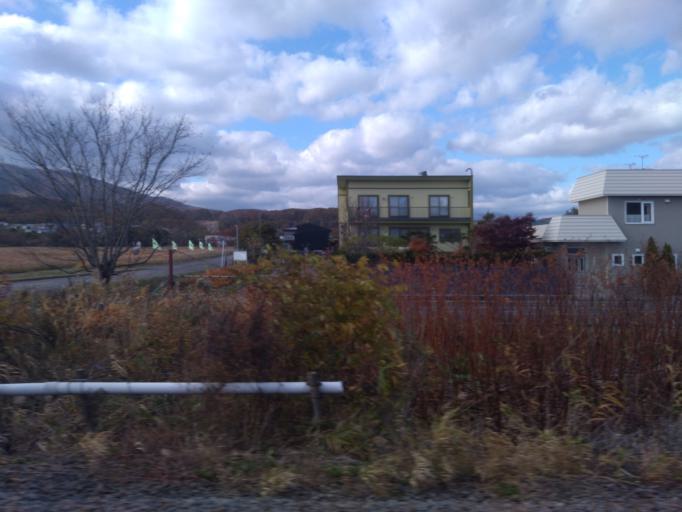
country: JP
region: Hokkaido
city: Shiraoi
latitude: 42.4864
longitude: 141.2498
